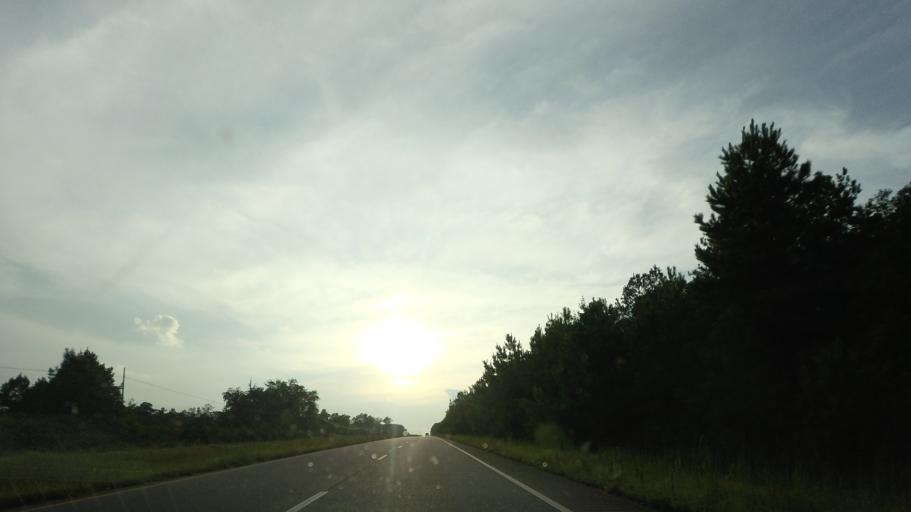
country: US
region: Georgia
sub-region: Wilkinson County
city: Gordon
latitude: 32.8482
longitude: -83.4261
